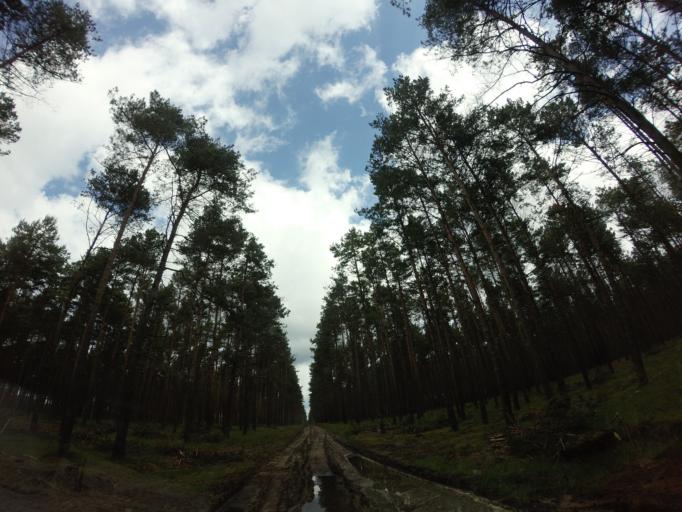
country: PL
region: West Pomeranian Voivodeship
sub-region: Powiat drawski
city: Kalisz Pomorski
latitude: 53.1835
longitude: 15.8995
